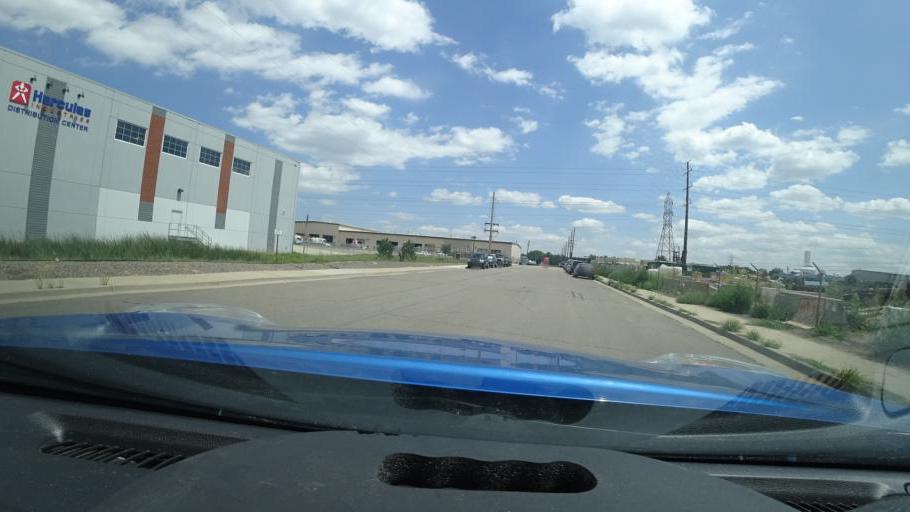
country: US
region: Colorado
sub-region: Arapahoe County
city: Englewood
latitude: 39.6748
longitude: -105.0039
